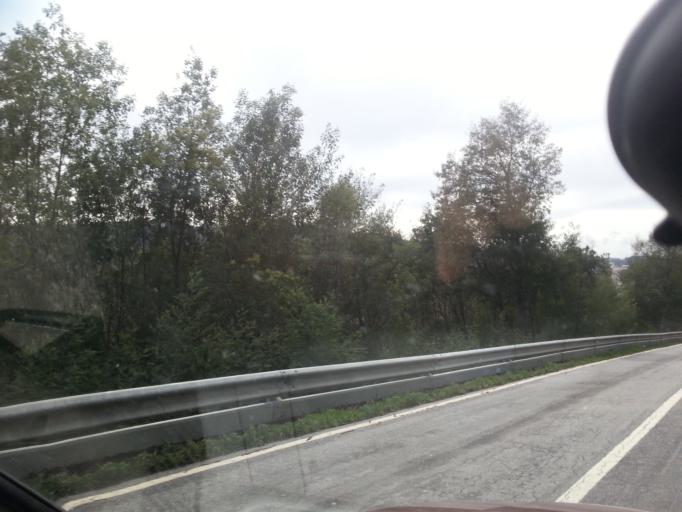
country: PT
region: Guarda
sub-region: Seia
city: Seia
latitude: 40.4384
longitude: -7.7099
